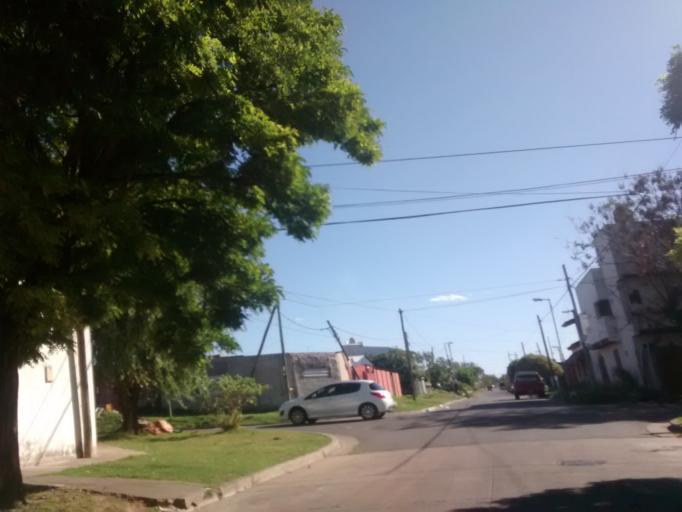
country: AR
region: Buenos Aires
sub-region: Partido de La Plata
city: La Plata
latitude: -34.9245
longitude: -57.9136
